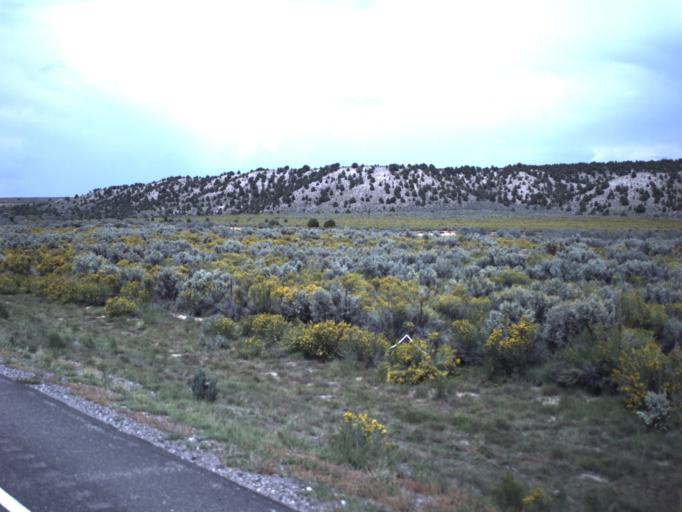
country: US
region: Utah
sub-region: Garfield County
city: Panguitch
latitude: 37.7549
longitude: -112.3793
